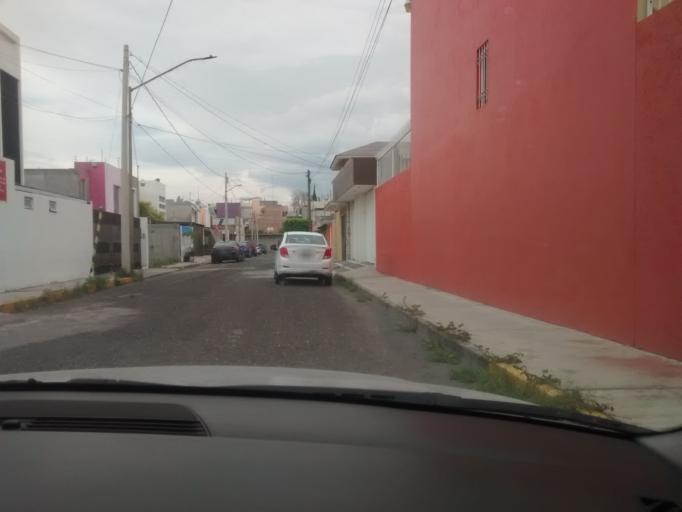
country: MX
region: Puebla
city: Tehuacan
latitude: 18.4613
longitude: -97.4102
